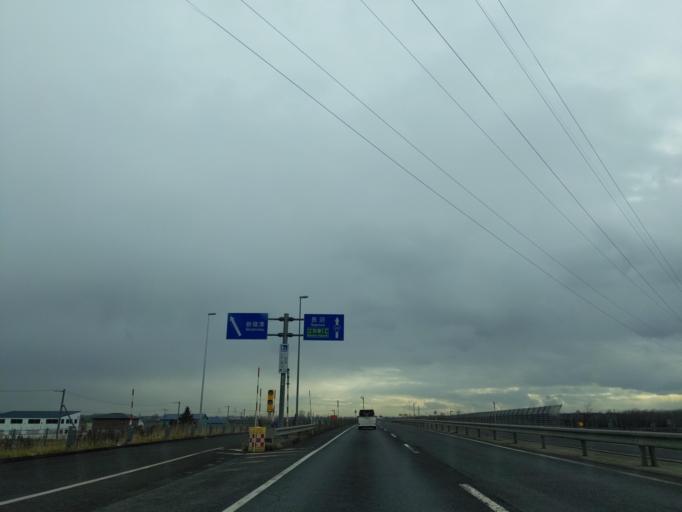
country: JP
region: Hokkaido
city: Ebetsu
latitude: 43.1596
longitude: 141.5651
